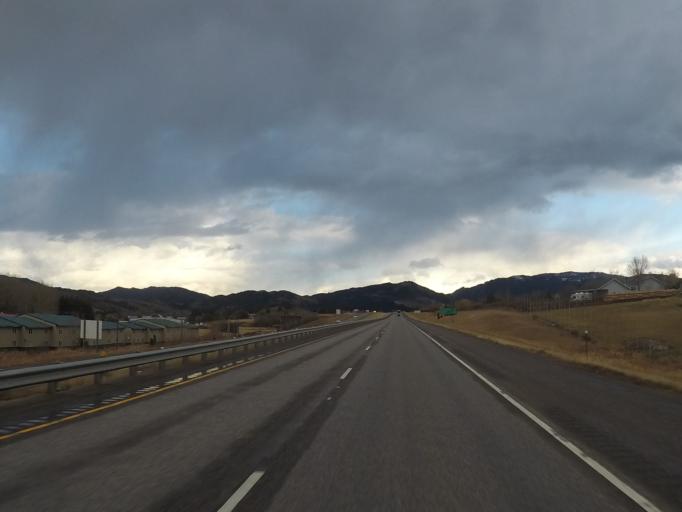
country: US
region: Montana
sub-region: Gallatin County
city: Bozeman
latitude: 45.6702
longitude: -110.9971
